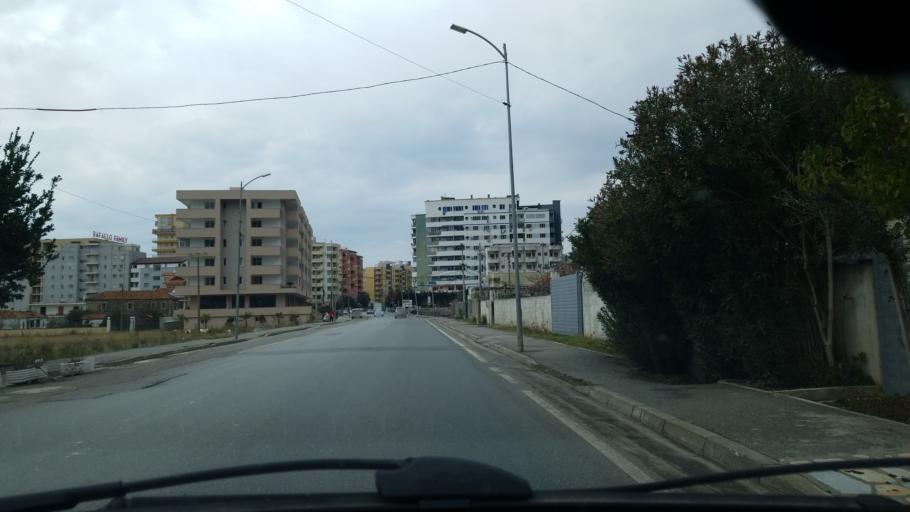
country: AL
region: Lezhe
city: Shengjin
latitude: 41.8086
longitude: 19.6036
